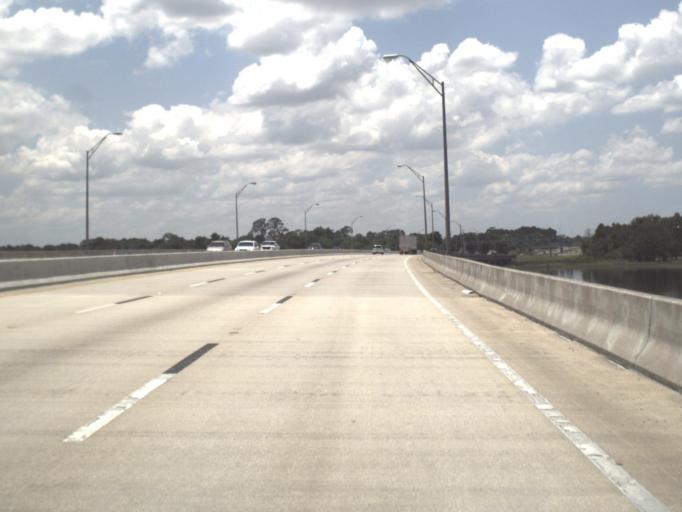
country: US
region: Florida
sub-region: Duval County
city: Jacksonville
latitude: 30.3696
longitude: -81.5517
